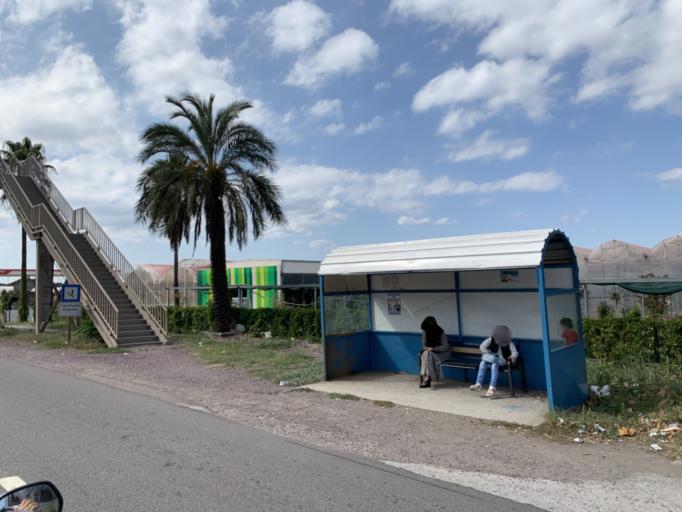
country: TR
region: Yalova
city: Taskopru
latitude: 40.6872
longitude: 29.4443
